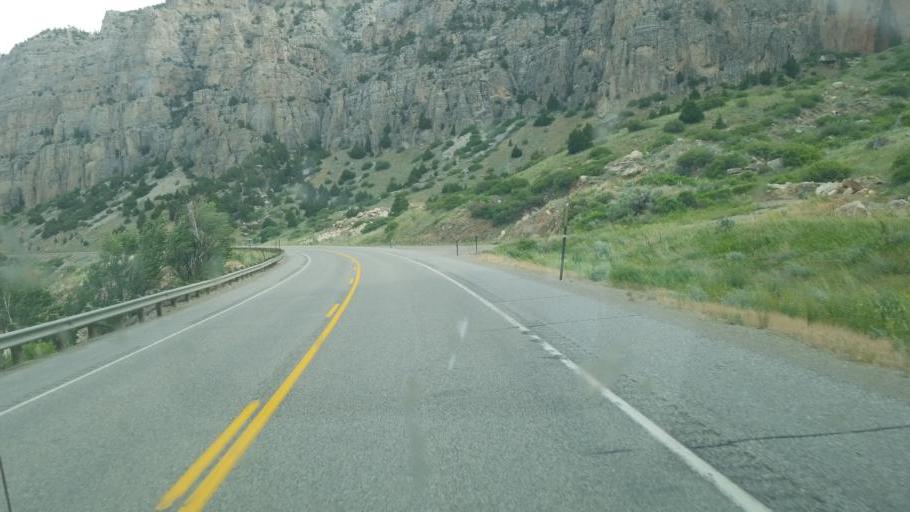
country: US
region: Wyoming
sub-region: Hot Springs County
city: Thermopolis
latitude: 43.5247
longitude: -108.1750
